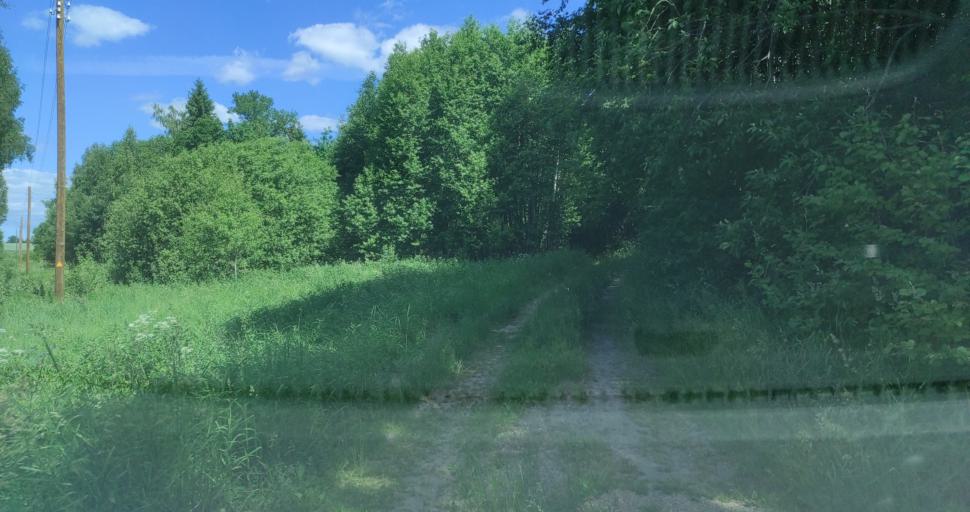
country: LV
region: Aizpute
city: Aizpute
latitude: 56.8615
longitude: 21.7291
